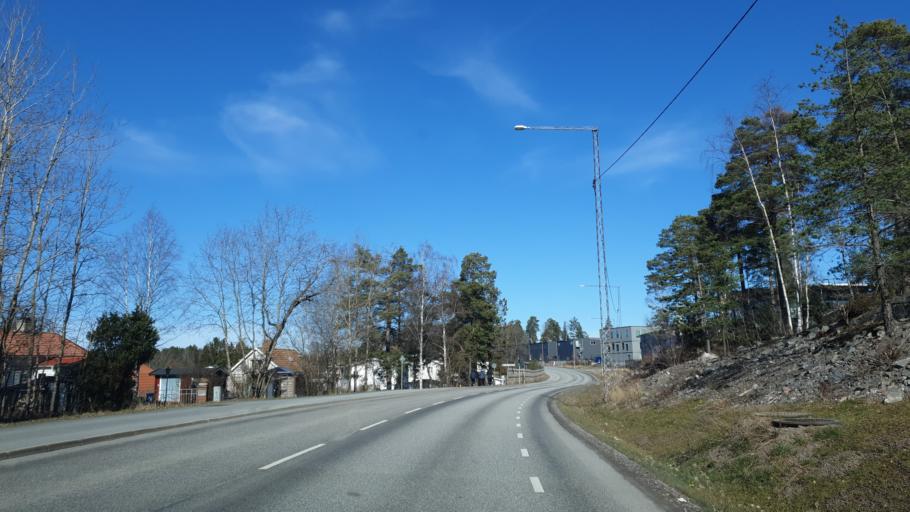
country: SE
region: Stockholm
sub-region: Jarfalla Kommun
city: Jakobsberg
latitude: 59.4432
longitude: 17.8390
